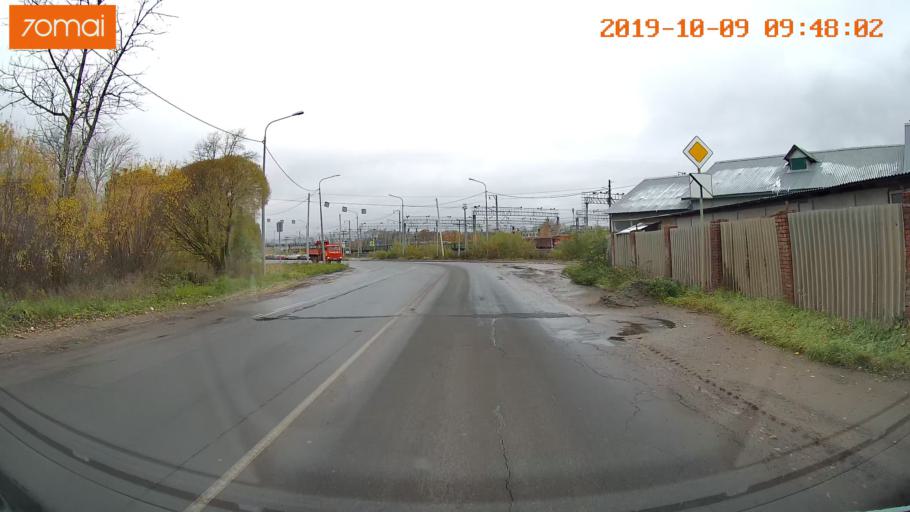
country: RU
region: Vologda
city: Vologda
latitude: 59.1927
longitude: 39.9339
